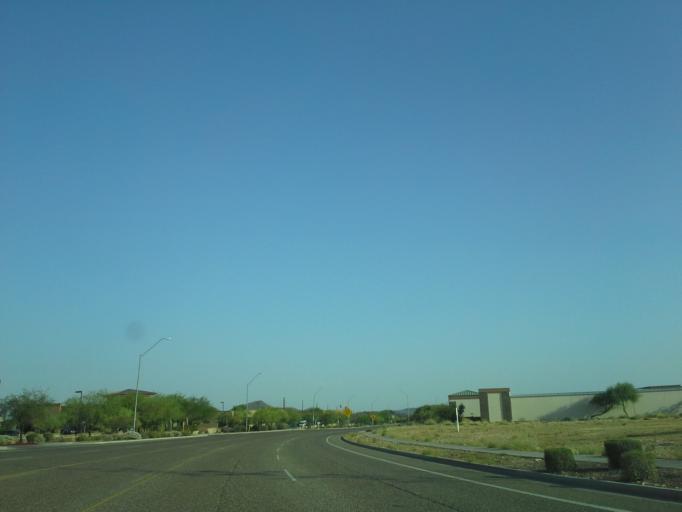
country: US
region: Arizona
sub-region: Maricopa County
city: Anthem
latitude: 33.8680
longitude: -112.1508
